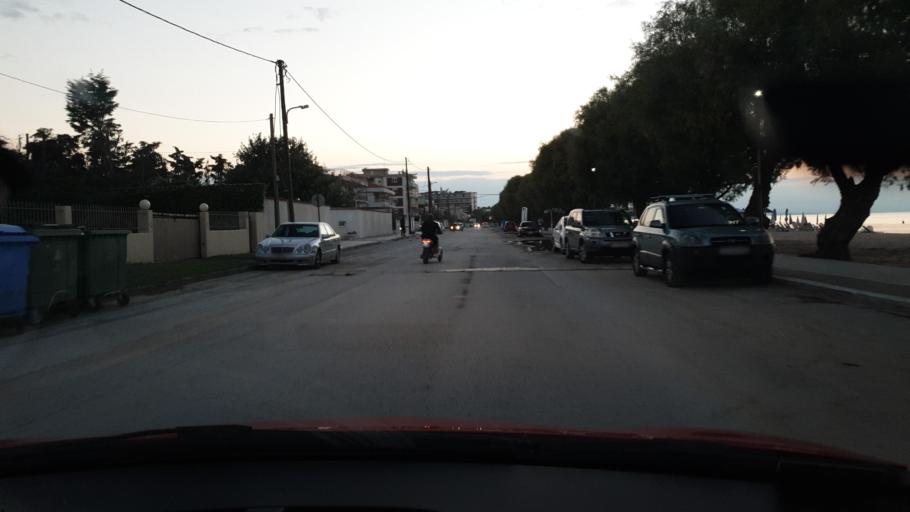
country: GR
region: Central Macedonia
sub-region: Nomos Thessalonikis
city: Neoi Epivates
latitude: 40.5035
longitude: 22.9012
